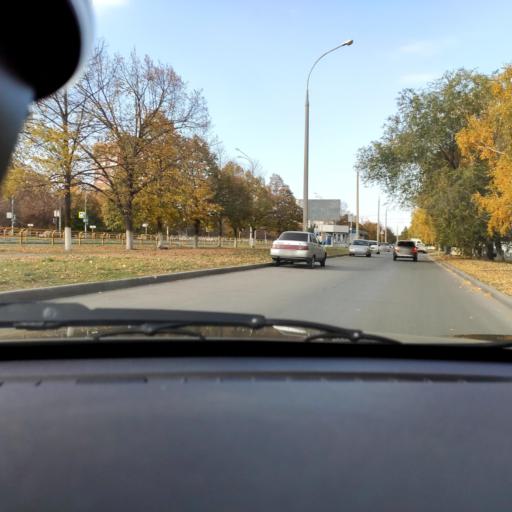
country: RU
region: Samara
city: Tol'yatti
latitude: 53.5260
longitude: 49.3190
